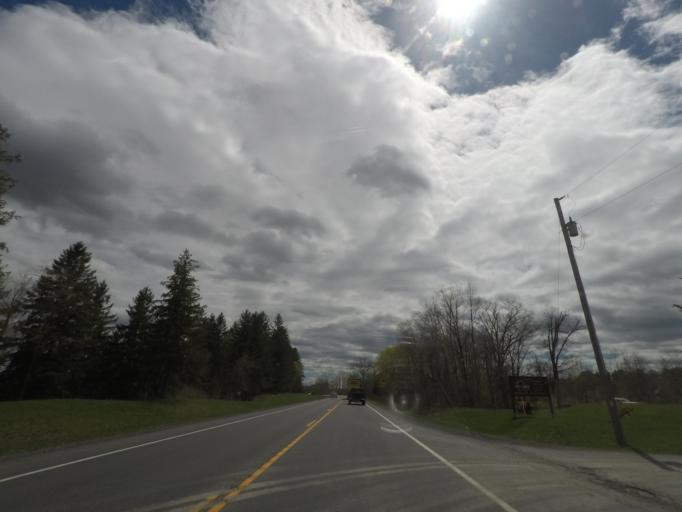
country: US
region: New York
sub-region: Albany County
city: Ravena
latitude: 42.4832
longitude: -73.7938
